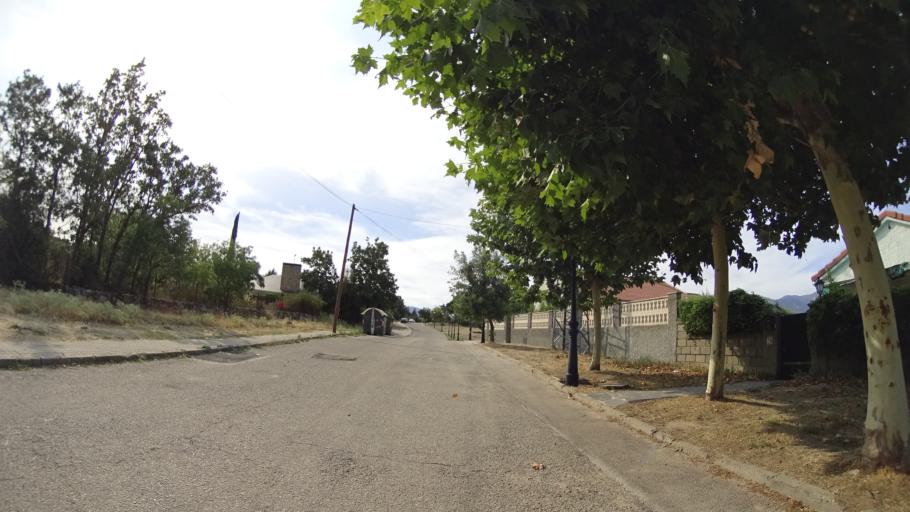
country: ES
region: Madrid
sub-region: Provincia de Madrid
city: Becerril de la Sierra
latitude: 40.7024
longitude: -3.9857
